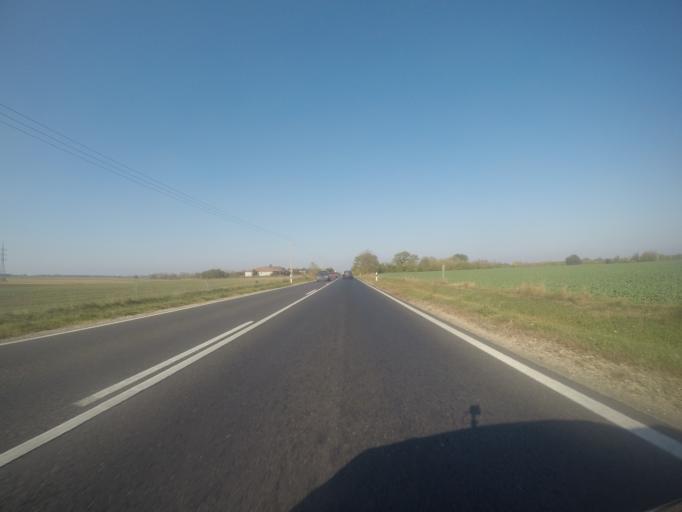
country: HU
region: Fejer
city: Baracs
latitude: 46.8480
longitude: 18.9113
